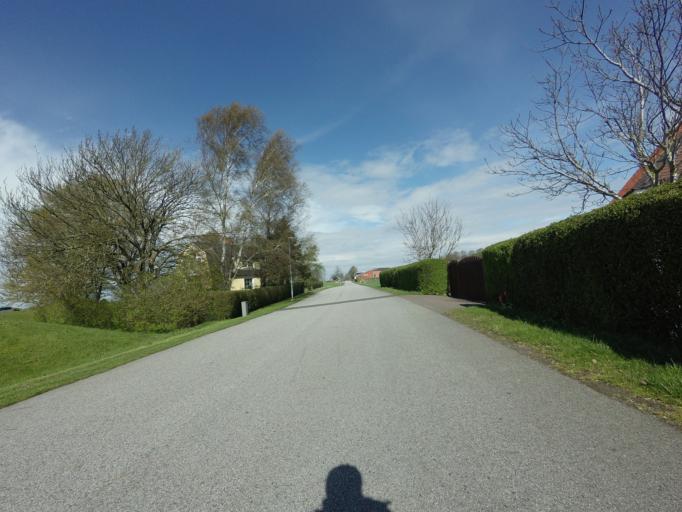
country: SE
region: Skane
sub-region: Vellinge Kommun
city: Vellinge
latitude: 55.4914
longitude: 13.0048
